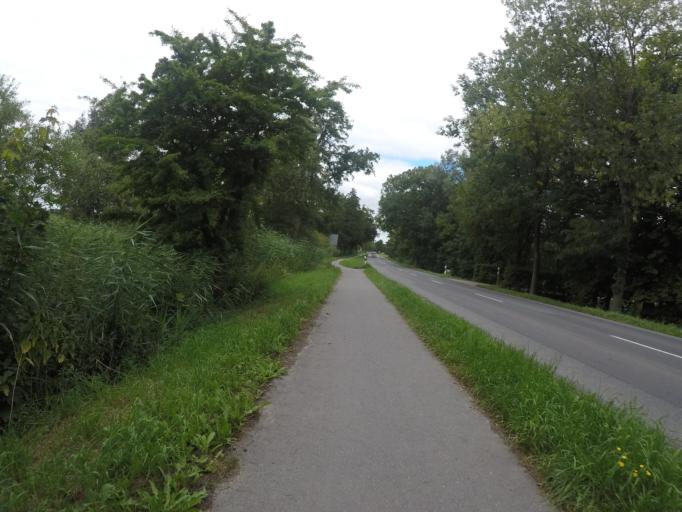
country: DE
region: Lower Saxony
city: Grossenworden
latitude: 53.6606
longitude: 9.2944
